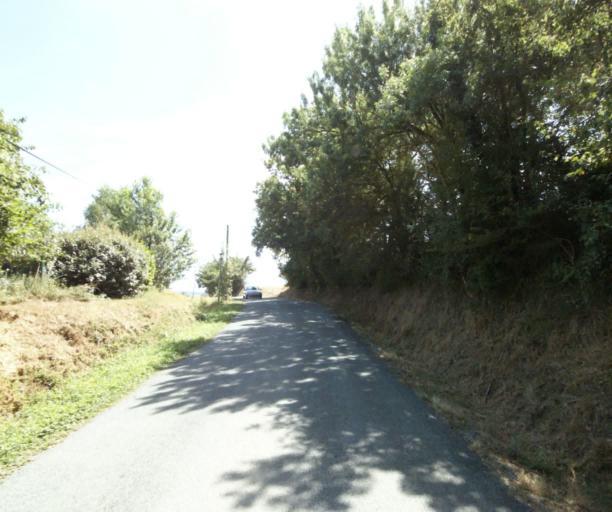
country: FR
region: Midi-Pyrenees
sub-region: Departement de la Haute-Garonne
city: Revel
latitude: 43.4942
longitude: 2.0215
